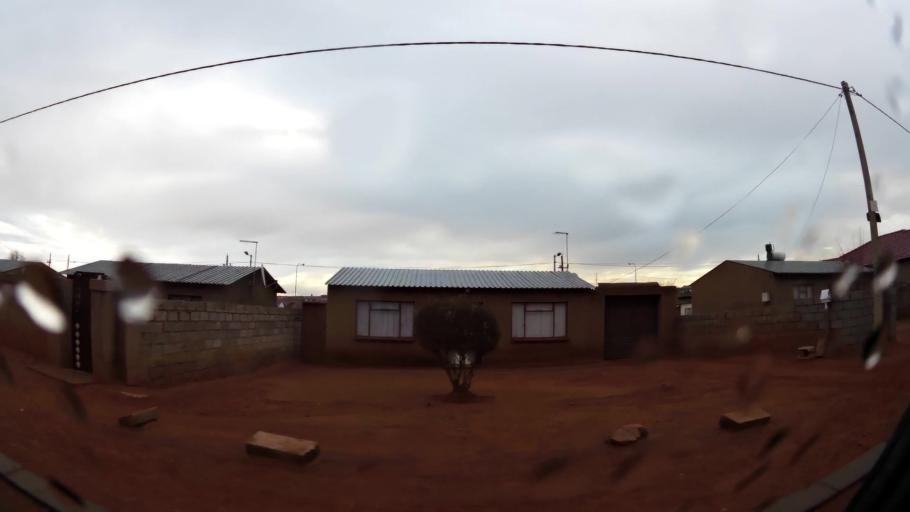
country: ZA
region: Gauteng
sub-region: West Rand District Municipality
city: Randfontein
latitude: -26.1733
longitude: 27.7830
